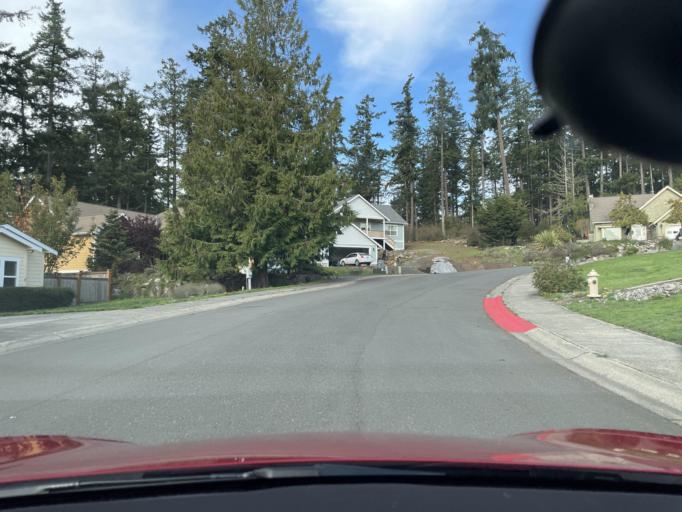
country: US
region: Washington
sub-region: San Juan County
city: Friday Harbor
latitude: 48.5427
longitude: -123.0333
